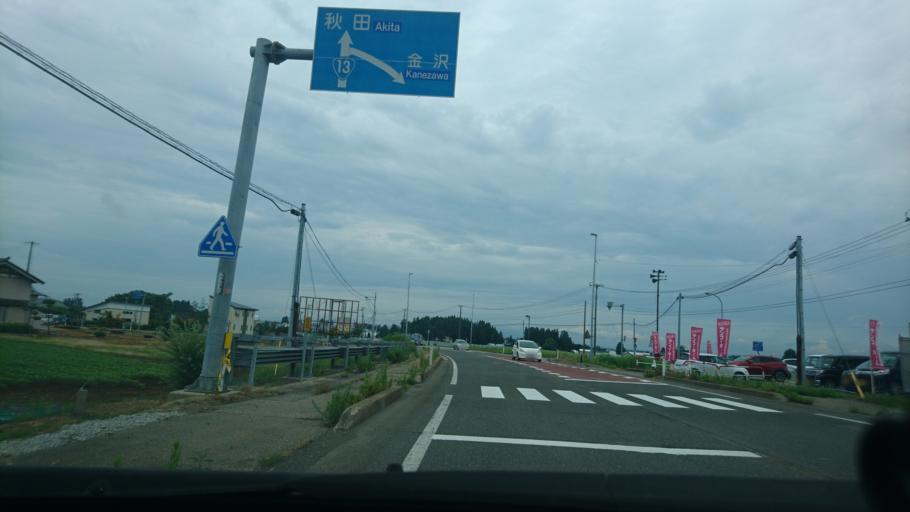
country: JP
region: Akita
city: Yokotemachi
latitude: 39.3912
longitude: 140.5684
